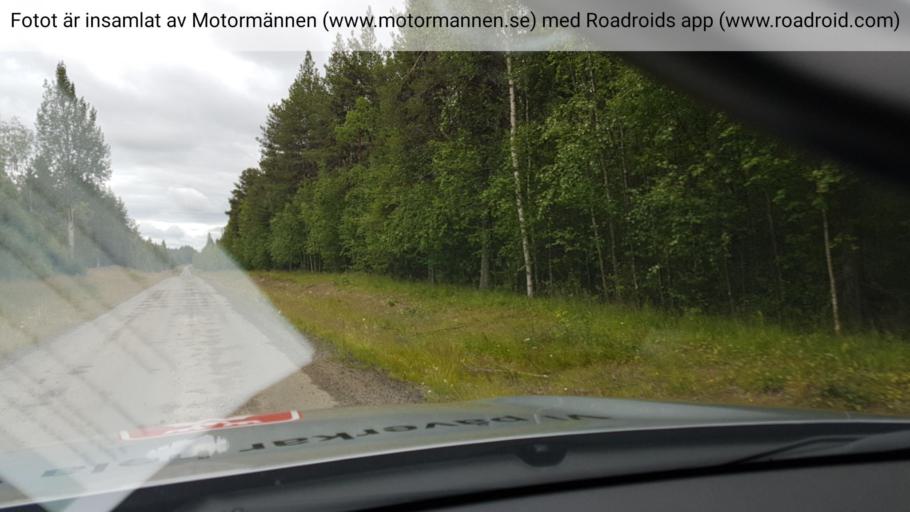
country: SE
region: Norrbotten
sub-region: Pajala Kommun
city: Pajala
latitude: 66.9783
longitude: 22.8924
